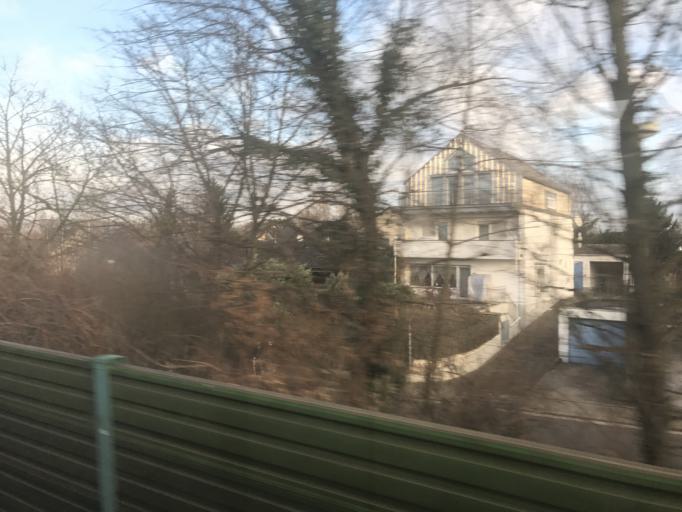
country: DE
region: Rheinland-Pfalz
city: Weissenthurm
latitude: 50.4233
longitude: 7.4481
